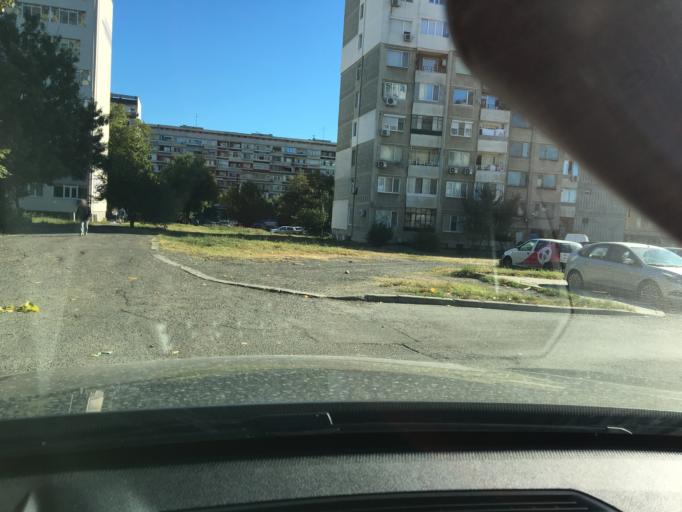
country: BG
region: Burgas
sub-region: Obshtina Burgas
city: Burgas
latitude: 42.5216
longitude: 27.4526
